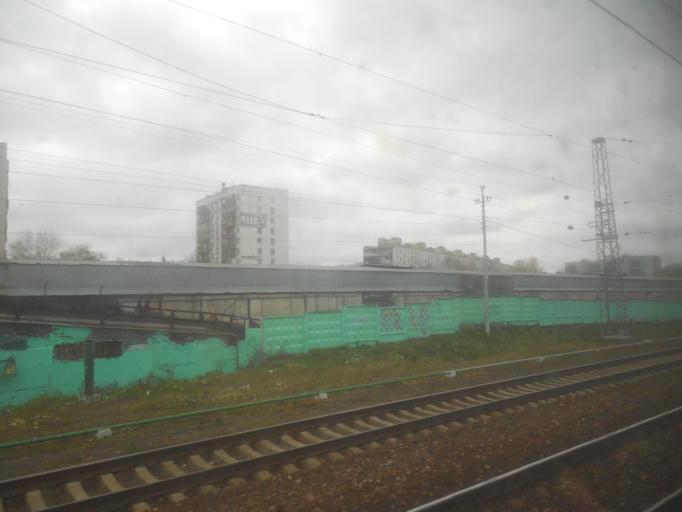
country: RU
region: Moskovskaya
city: Bol'shaya Setun'
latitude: 55.7269
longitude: 37.4362
